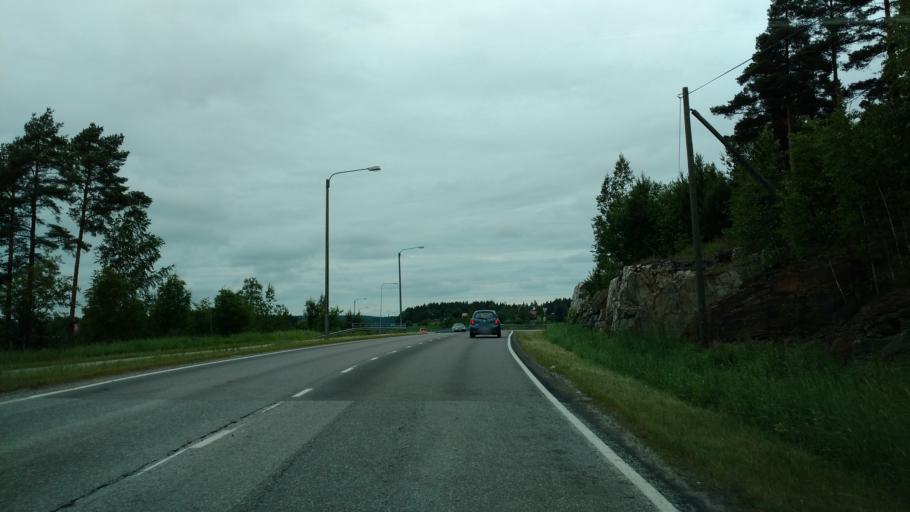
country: FI
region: Varsinais-Suomi
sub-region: Salo
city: Halikko
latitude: 60.4117
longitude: 23.0554
